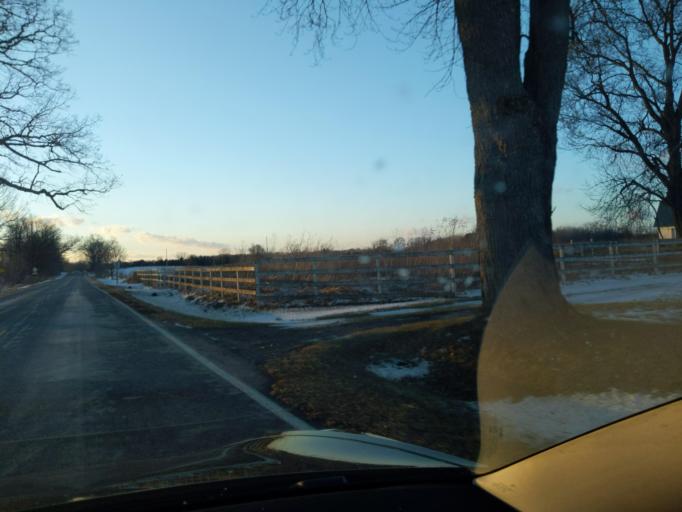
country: US
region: Michigan
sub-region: Ingham County
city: Stockbridge
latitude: 42.4467
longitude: -84.2150
